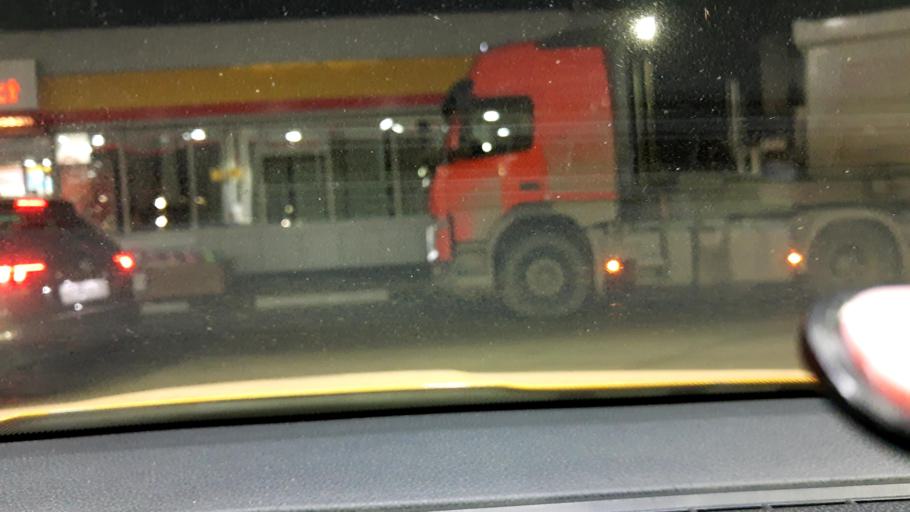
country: RU
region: Moskovskaya
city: Odintsovo
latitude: 55.6573
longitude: 37.2940
